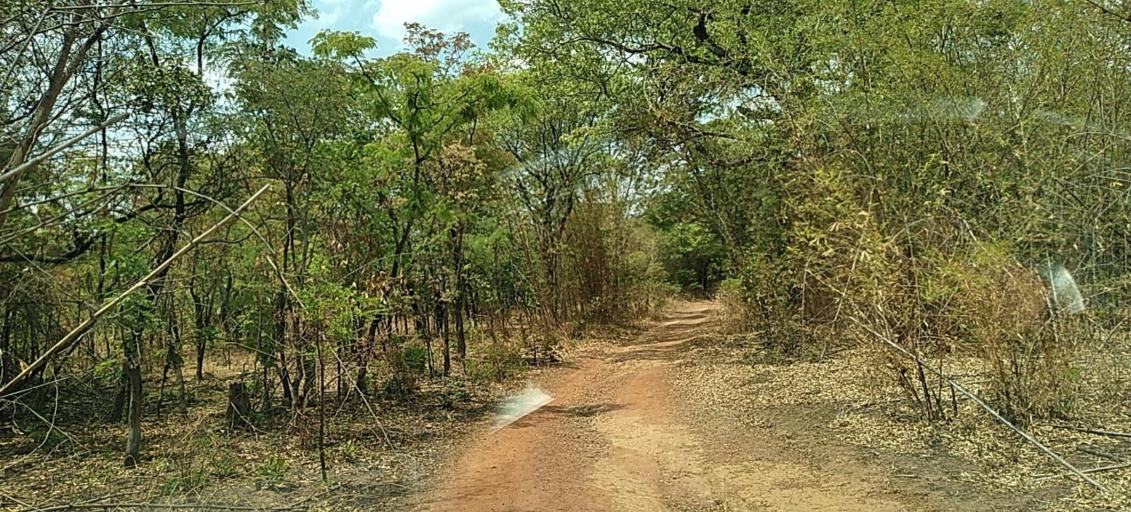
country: ZM
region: Copperbelt
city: Chililabombwe
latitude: -12.4787
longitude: 27.6452
